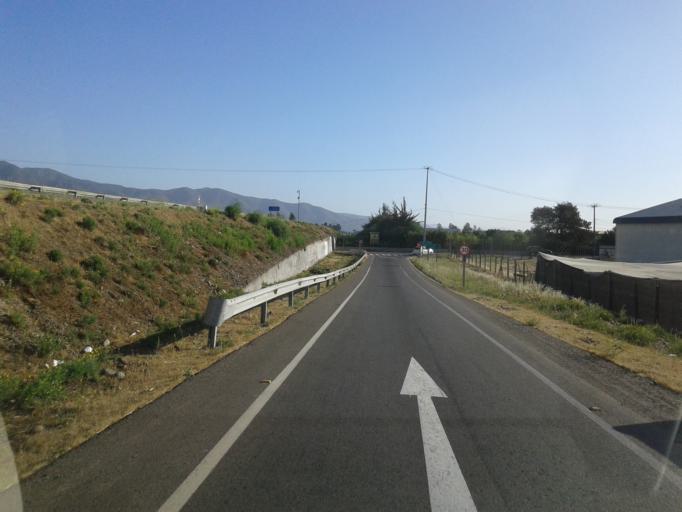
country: CL
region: Valparaiso
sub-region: Provincia de Quillota
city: Quillota
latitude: -32.8577
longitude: -71.2250
